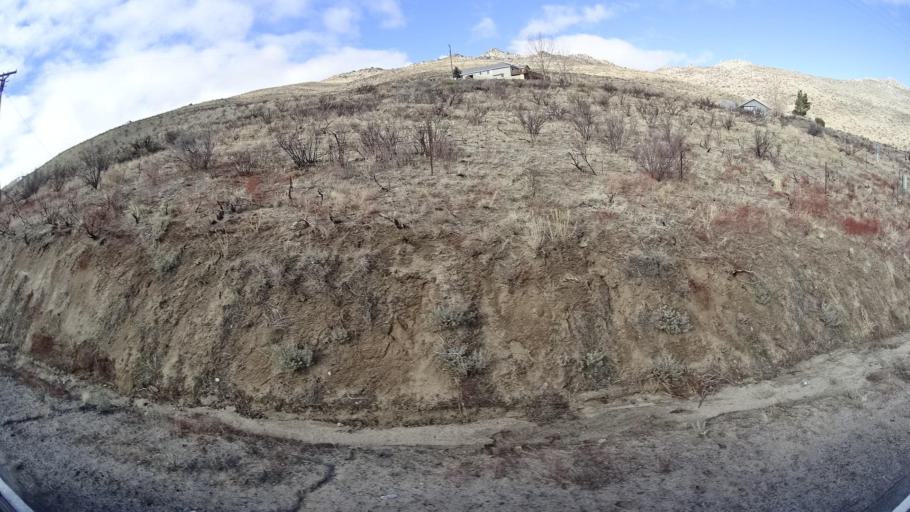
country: US
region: Nevada
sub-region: Washoe County
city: Cold Springs
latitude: 39.8448
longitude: -119.9350
